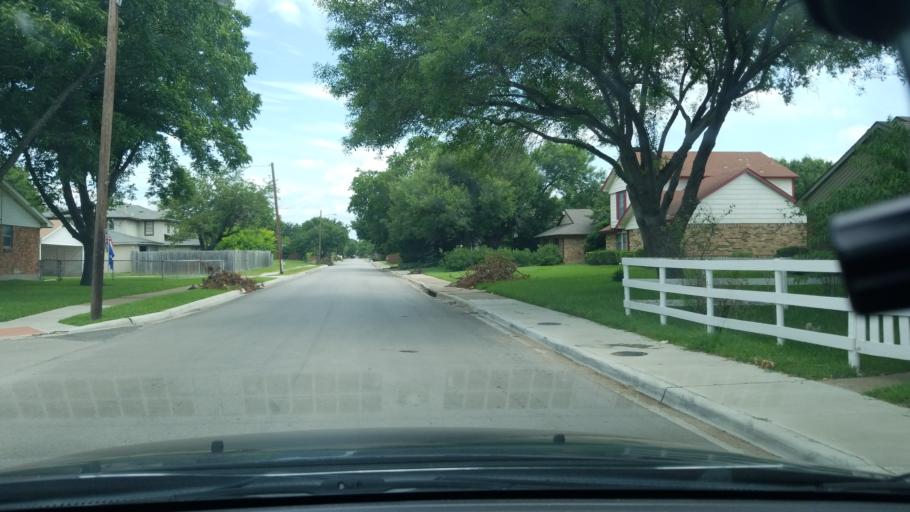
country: US
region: Texas
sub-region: Dallas County
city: Mesquite
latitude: 32.8150
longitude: -96.6684
